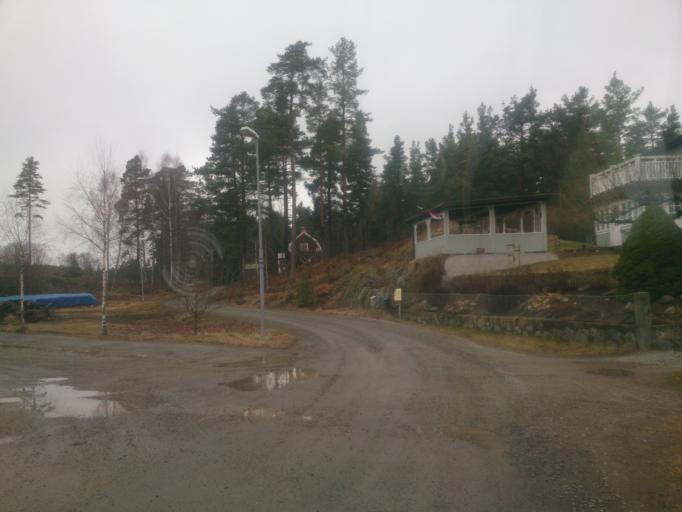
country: SE
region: OEstergoetland
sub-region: Atvidabergs Kommun
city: Atvidaberg
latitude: 58.2193
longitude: 16.0233
